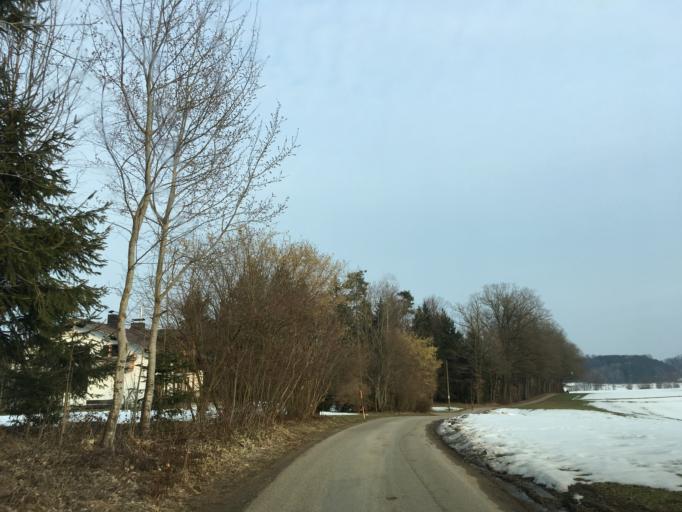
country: DE
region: Bavaria
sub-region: Upper Bavaria
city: Halfing
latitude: 47.9427
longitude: 12.2682
